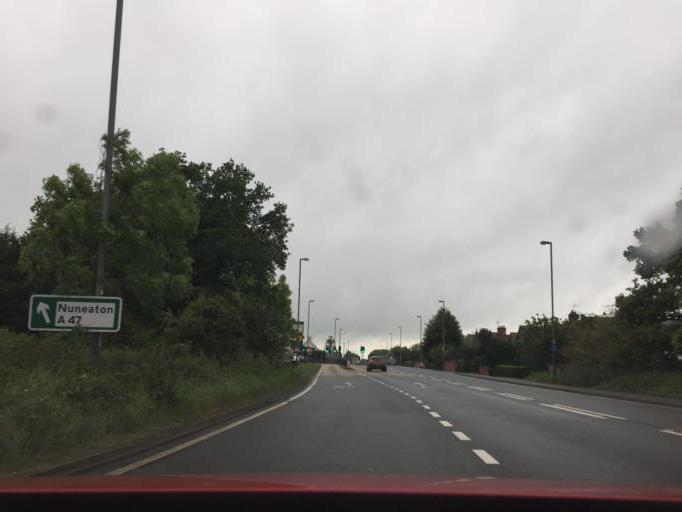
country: GB
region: England
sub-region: Leicestershire
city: Stoke Golding
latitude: 52.5363
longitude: -1.4184
